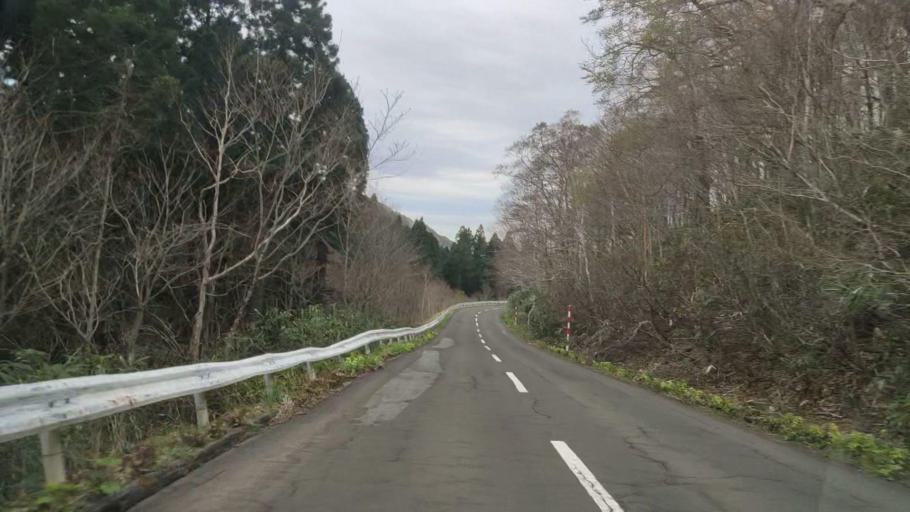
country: JP
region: Akita
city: Hanawa
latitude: 40.4105
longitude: 140.8174
